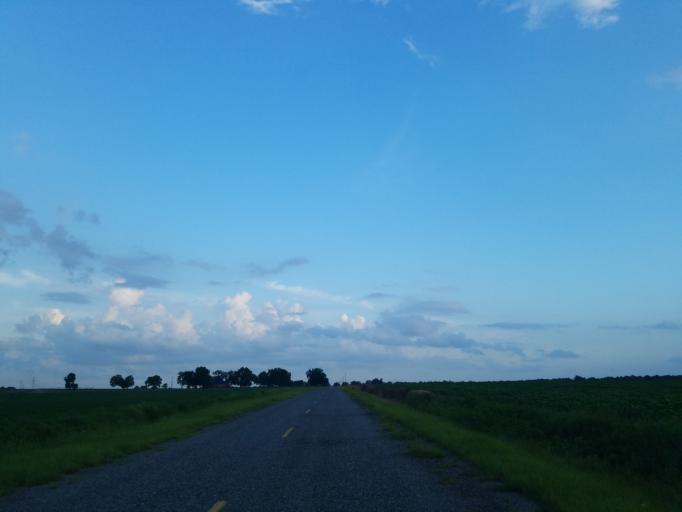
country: US
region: Georgia
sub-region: Dooly County
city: Unadilla
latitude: 32.1707
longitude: -83.7209
